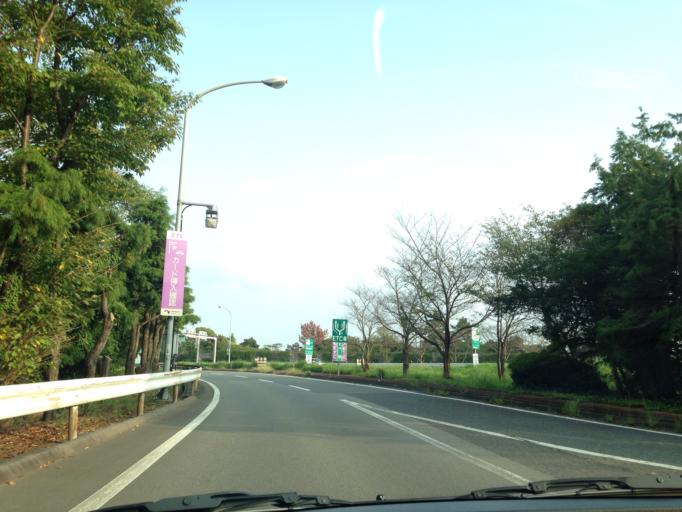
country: JP
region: Aichi
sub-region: Tokai-shi
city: Toyokawa
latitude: 34.8370
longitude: 137.4108
